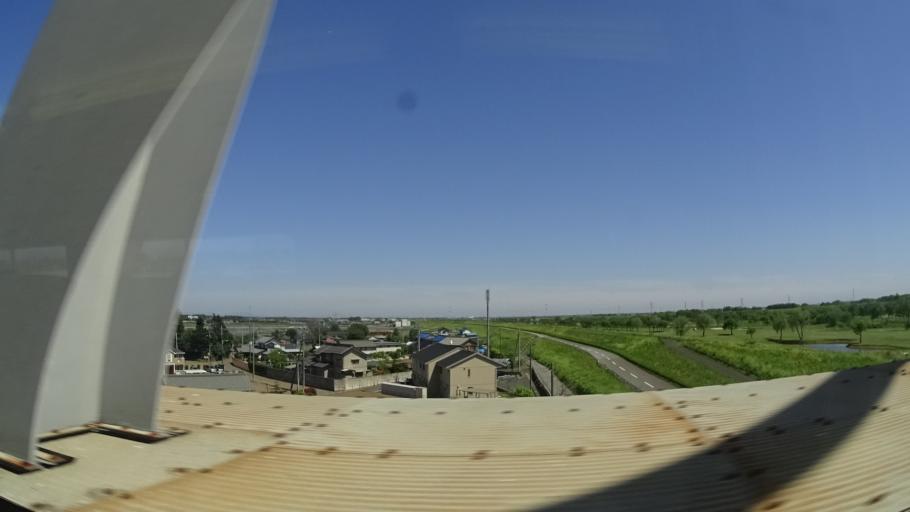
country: JP
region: Saitama
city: Kurihashi
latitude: 36.1386
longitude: 139.7213
